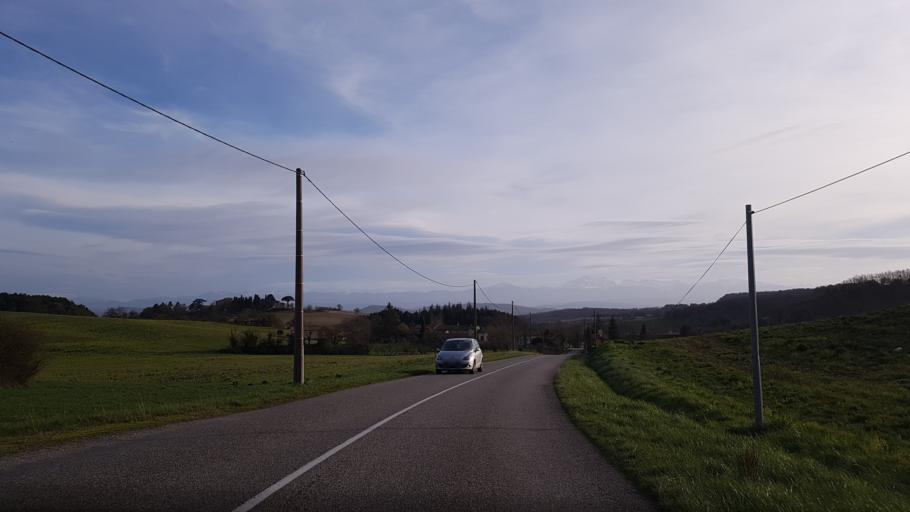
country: FR
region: Midi-Pyrenees
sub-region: Departement de l'Ariege
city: Mirepoix
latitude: 43.1324
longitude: 1.9153
